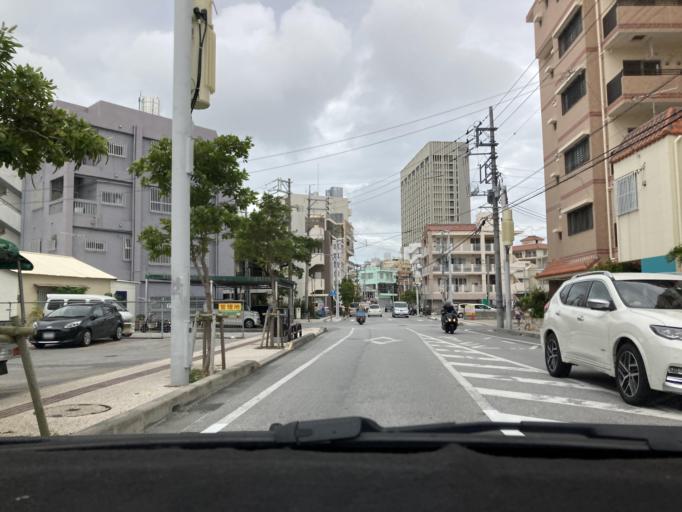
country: JP
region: Okinawa
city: Naha-shi
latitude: 26.2121
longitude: 127.6908
